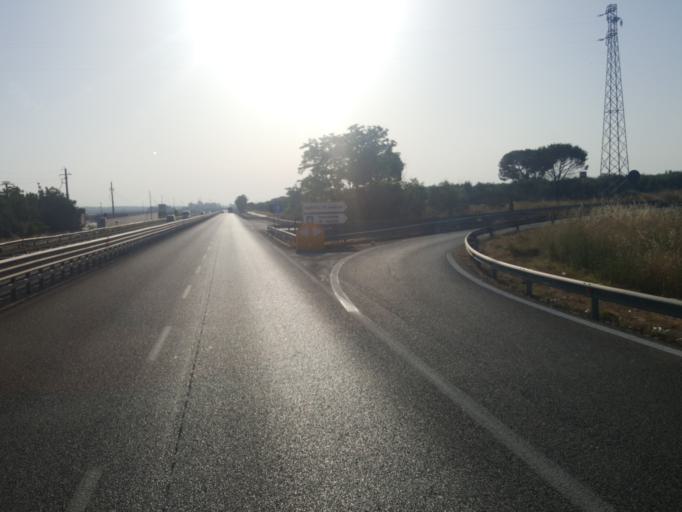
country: IT
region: Apulia
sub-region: Provincia di Foggia
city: Cerignola
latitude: 41.2699
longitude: 15.9528
